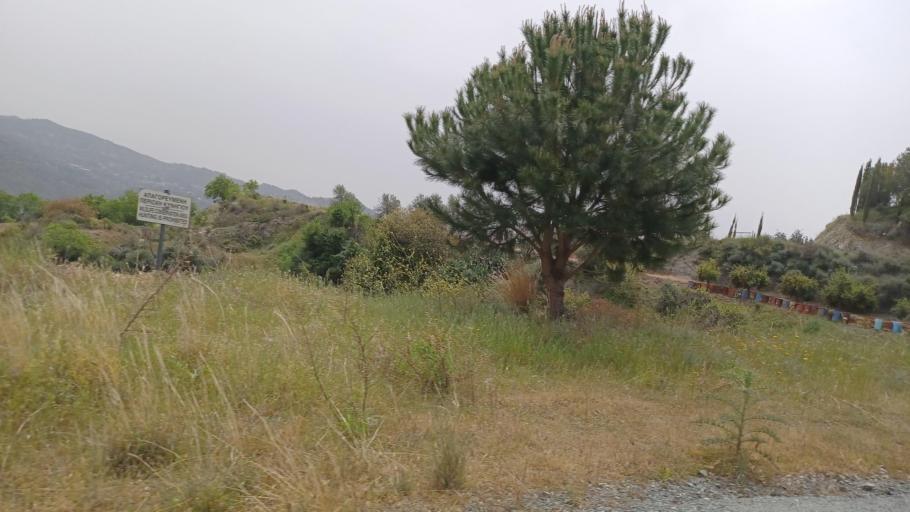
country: CY
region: Limassol
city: Parekklisha
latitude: 34.8325
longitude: 33.1014
